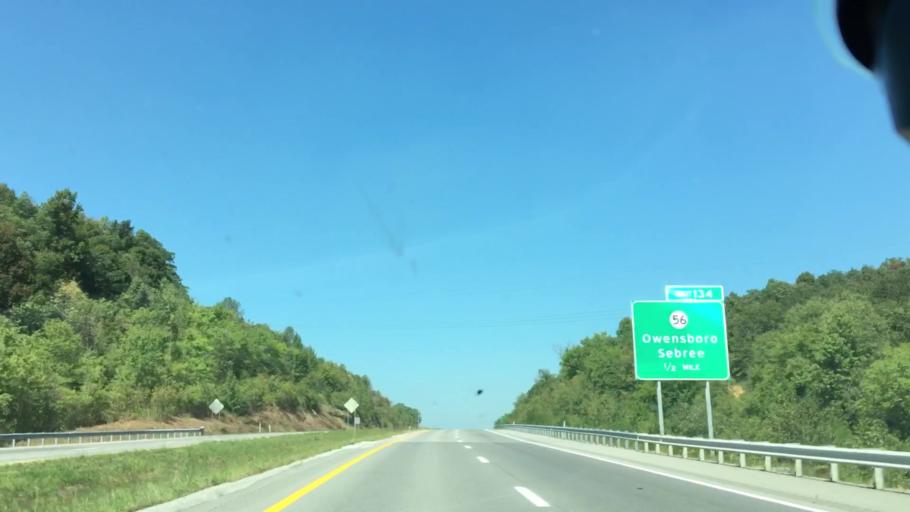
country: US
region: Kentucky
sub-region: Webster County
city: Sebree
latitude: 37.5985
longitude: -87.4958
